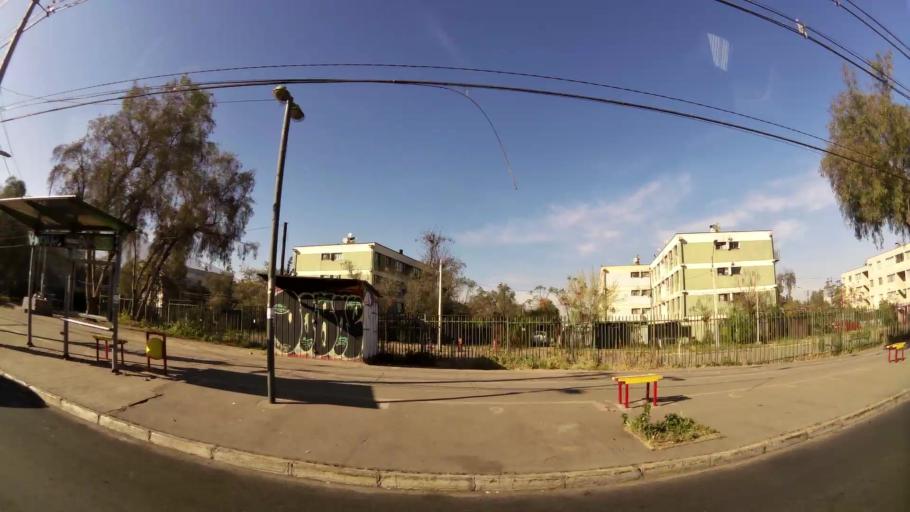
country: CL
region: Santiago Metropolitan
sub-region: Provincia de Santiago
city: Villa Presidente Frei, Nunoa, Santiago, Chile
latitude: -33.4626
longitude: -70.5567
